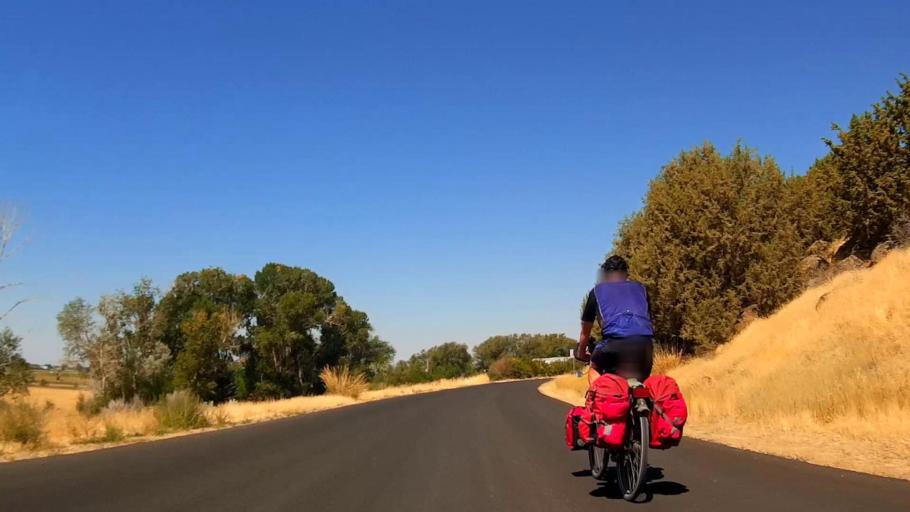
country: US
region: Idaho
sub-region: Madison County
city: Rexburg
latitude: 43.7153
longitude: -111.7542
